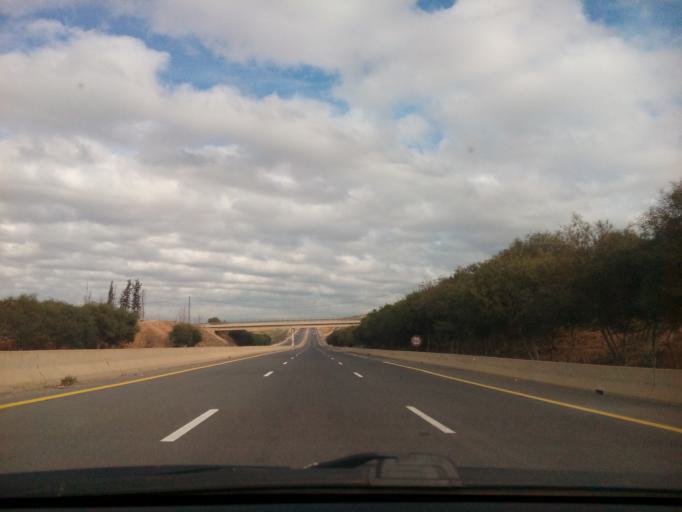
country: DZ
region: Tlemcen
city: Chetouane
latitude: 34.9500
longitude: -1.3037
